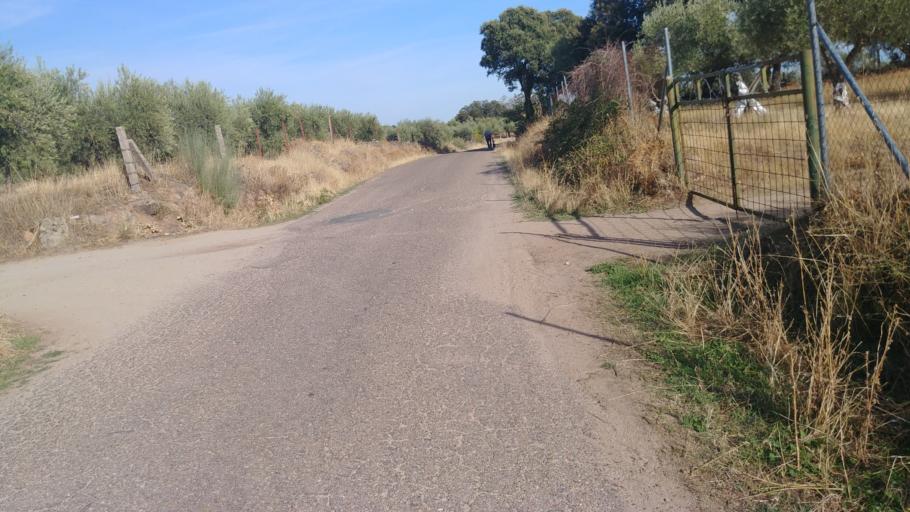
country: ES
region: Castille-La Mancha
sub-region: Province of Toledo
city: Navalcan
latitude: 40.0689
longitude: -5.1052
